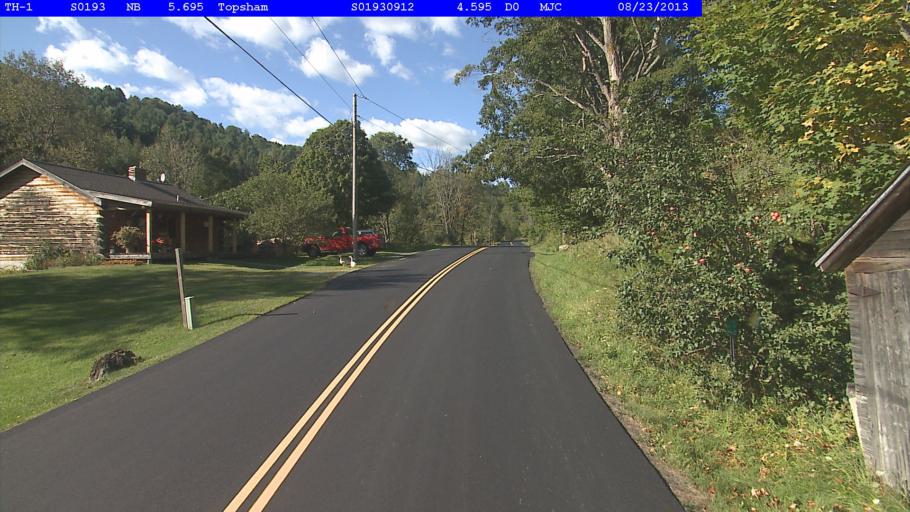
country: US
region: New Hampshire
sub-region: Grafton County
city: Haverhill
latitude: 44.1296
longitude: -72.2435
